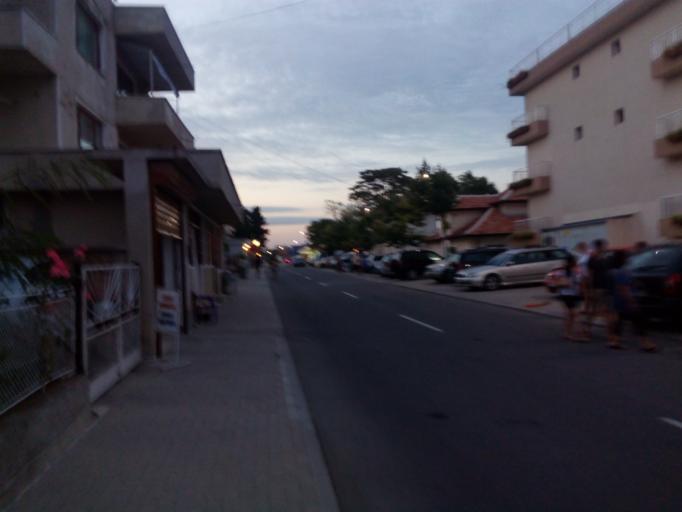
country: BG
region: Burgas
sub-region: Obshtina Nesebur
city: Obzor
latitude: 42.8184
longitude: 27.8844
